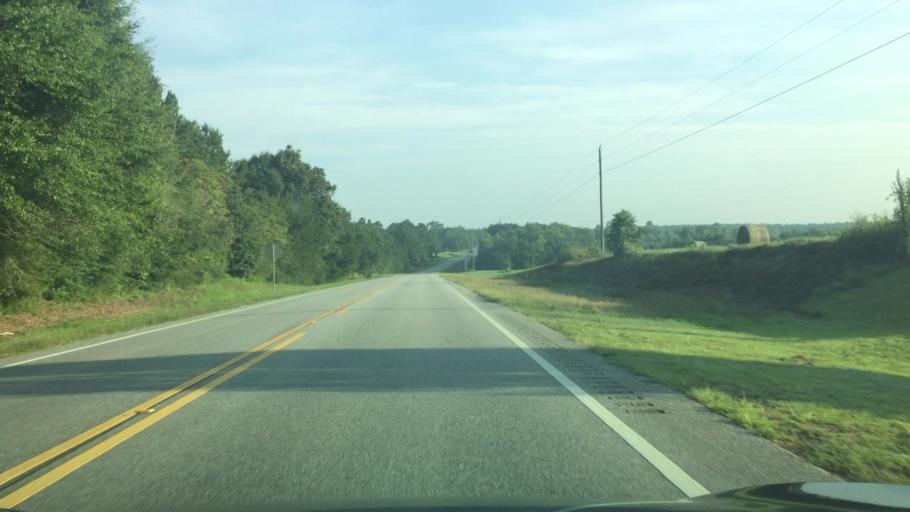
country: US
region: Alabama
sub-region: Covington County
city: Andalusia
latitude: 31.1336
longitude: -86.4583
